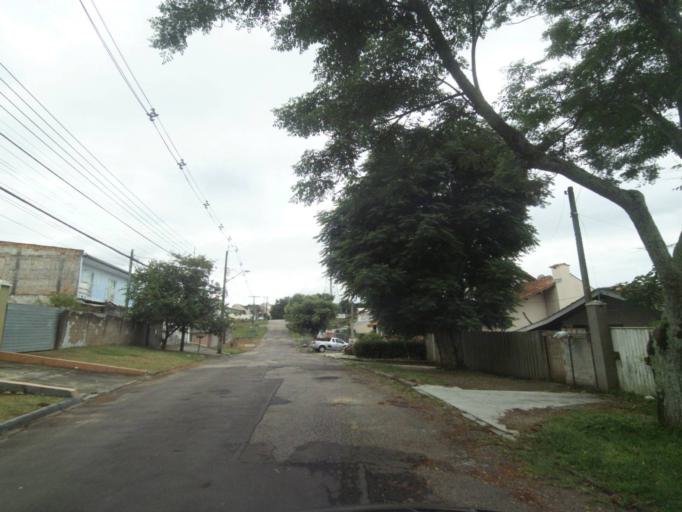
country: BR
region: Parana
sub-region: Curitiba
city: Curitiba
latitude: -25.4724
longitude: -49.3316
